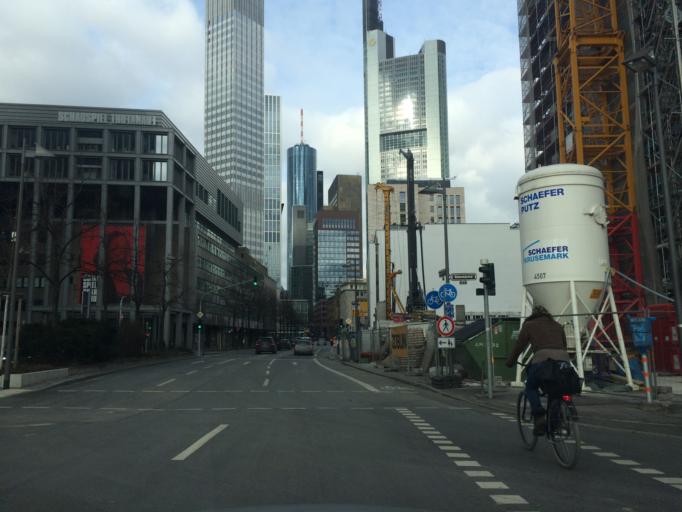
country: DE
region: Hesse
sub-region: Regierungsbezirk Darmstadt
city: Frankfurt am Main
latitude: 50.1075
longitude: 8.6759
